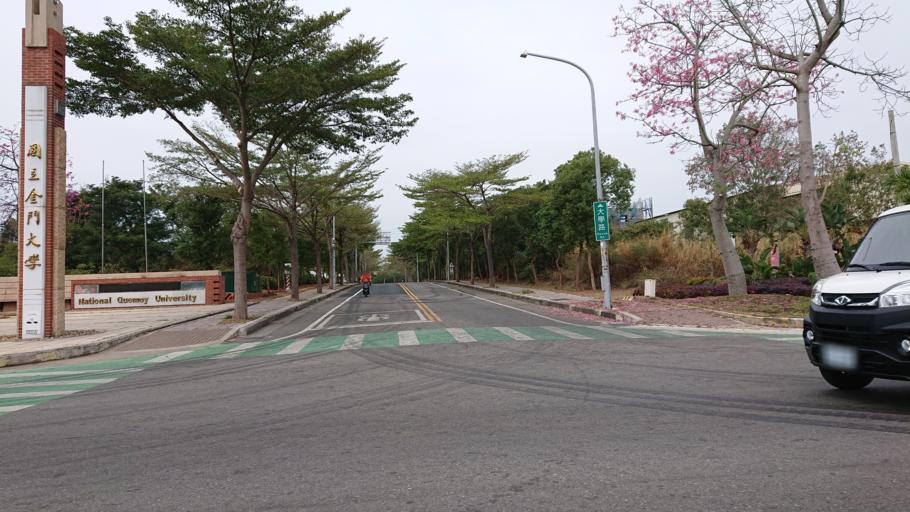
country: TW
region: Fukien
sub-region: Kinmen
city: Jincheng
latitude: 24.4449
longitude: 118.3269
